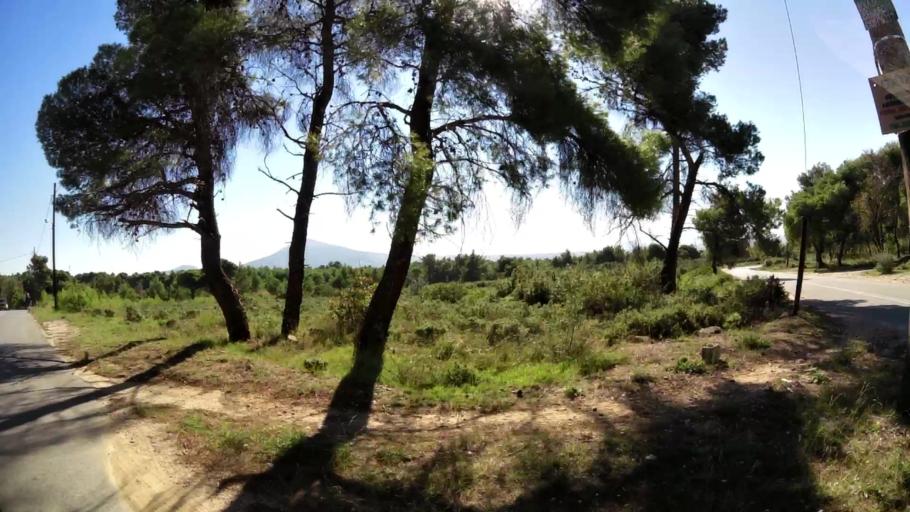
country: GR
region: Attica
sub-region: Nomarchia Anatolikis Attikis
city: Varybobi
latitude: 38.1334
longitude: 23.7765
